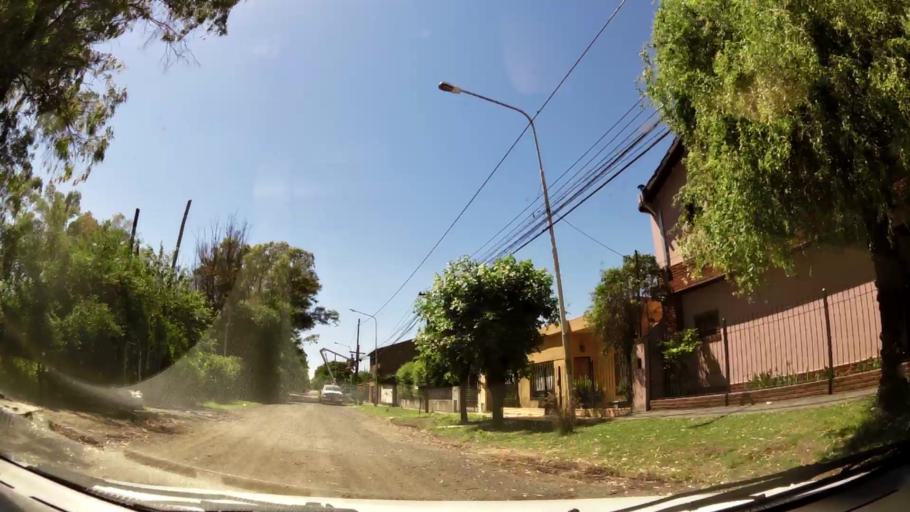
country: AR
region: Buenos Aires
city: Ituzaingo
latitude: -34.6732
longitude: -58.6615
